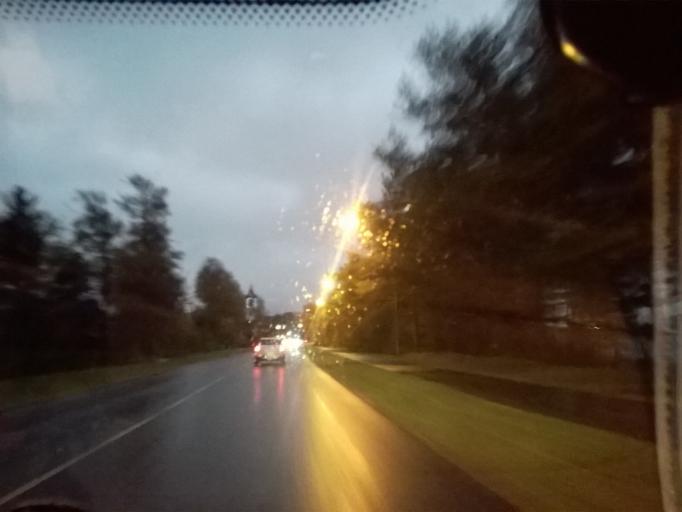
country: EE
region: Harju
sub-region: Viimsi vald
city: Haabneeme
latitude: 59.5191
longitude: 24.8097
